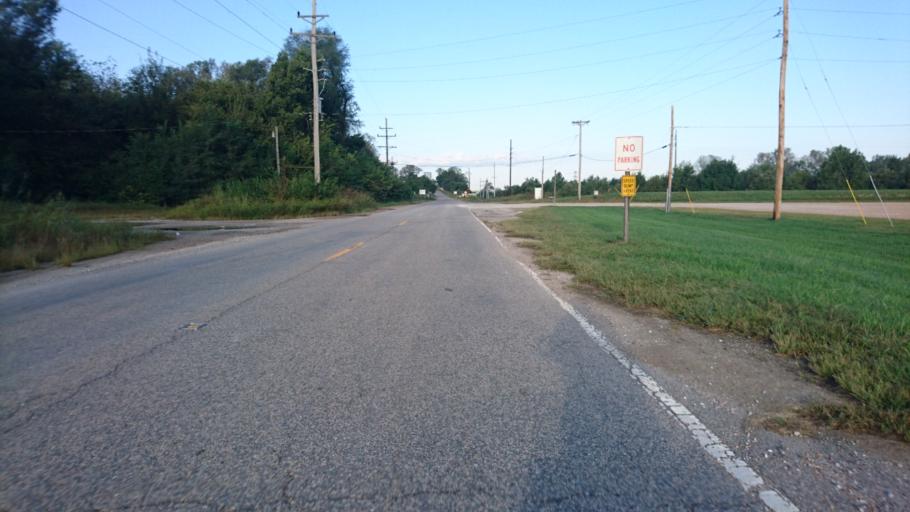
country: US
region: Illinois
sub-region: Madison County
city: Mitchell
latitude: 38.7622
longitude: -90.1285
